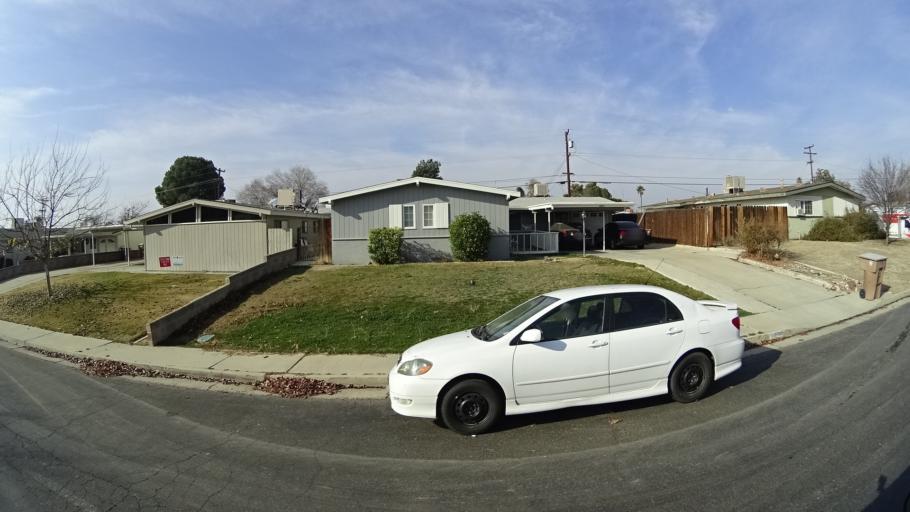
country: US
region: California
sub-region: Kern County
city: Oildale
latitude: 35.3997
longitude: -118.9686
